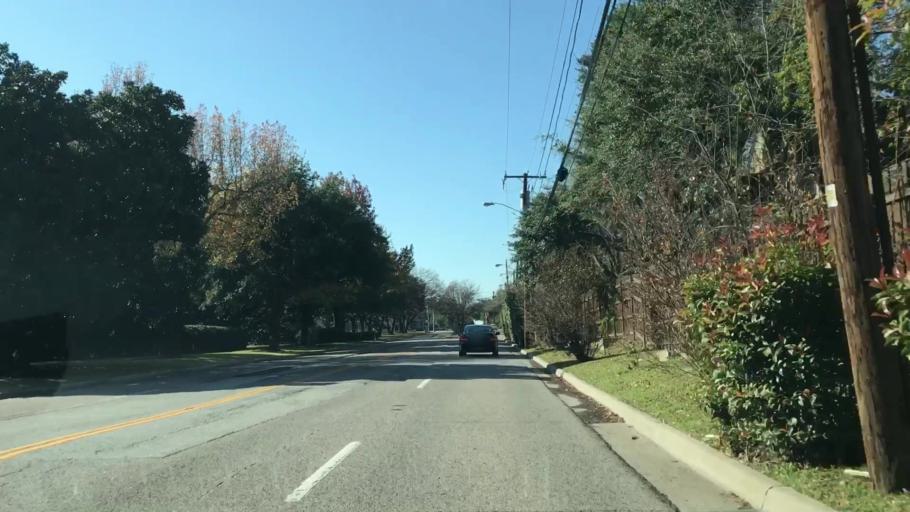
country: US
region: Texas
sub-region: Dallas County
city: University Park
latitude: 32.8735
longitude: -96.7841
